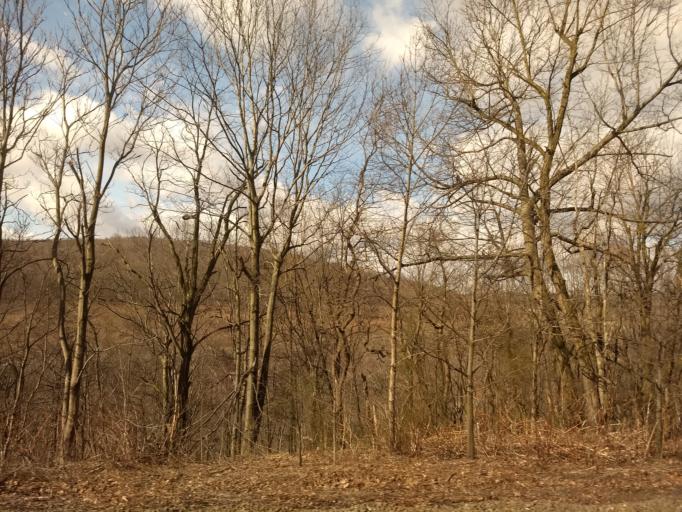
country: US
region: Pennsylvania
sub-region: Cambria County
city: Gallitzin
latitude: 40.4795
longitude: -78.5141
